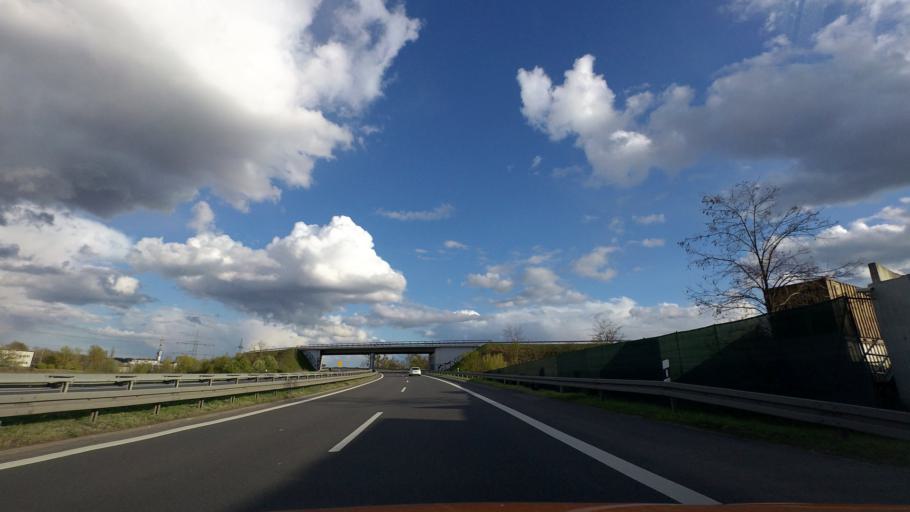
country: DE
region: Brandenburg
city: Wustermark
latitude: 52.5427
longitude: 12.9689
